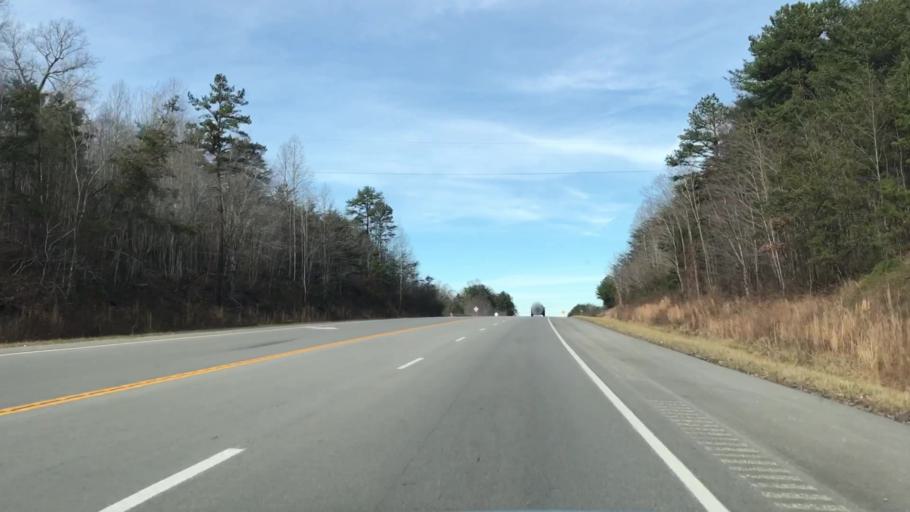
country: US
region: Kentucky
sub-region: McCreary County
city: Stearns
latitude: 36.6868
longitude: -84.4527
